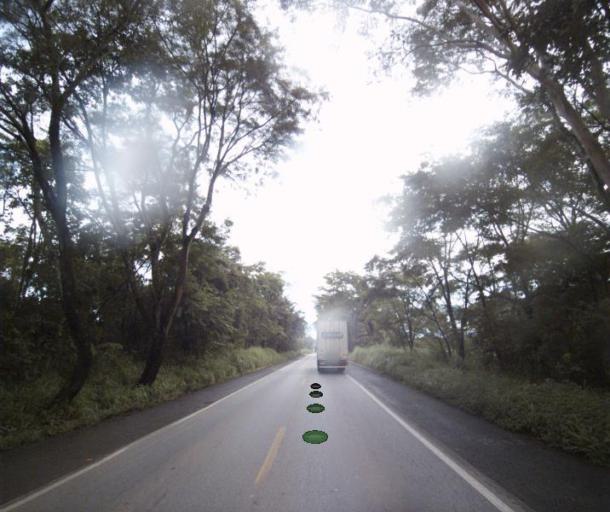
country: BR
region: Goias
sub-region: Porangatu
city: Porangatu
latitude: -13.9454
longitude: -49.0822
